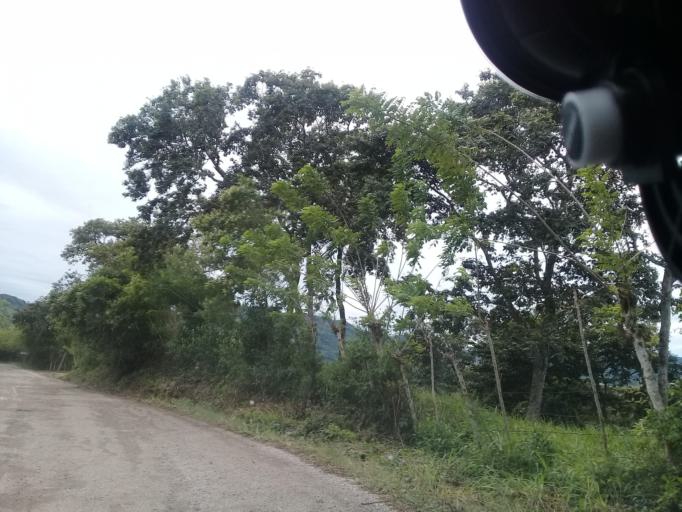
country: MX
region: Veracruz
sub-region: Chalma
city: San Pedro Coyutla
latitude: 21.2125
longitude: -98.3845
